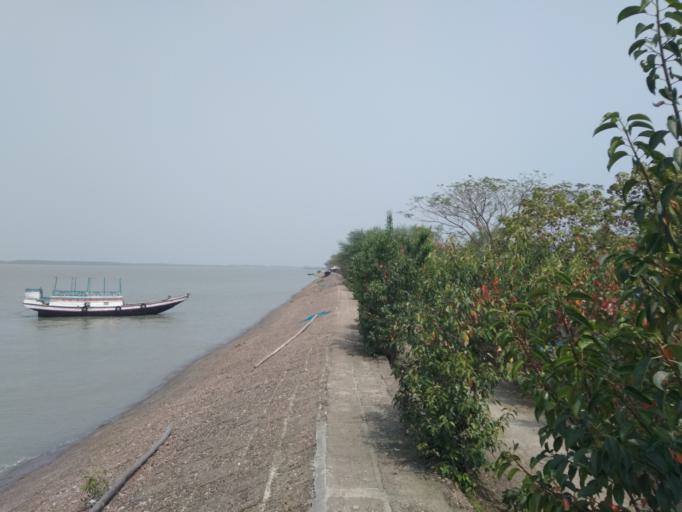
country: IN
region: West Bengal
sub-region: North 24 Parganas
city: Gosaba
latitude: 22.2525
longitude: 89.2504
